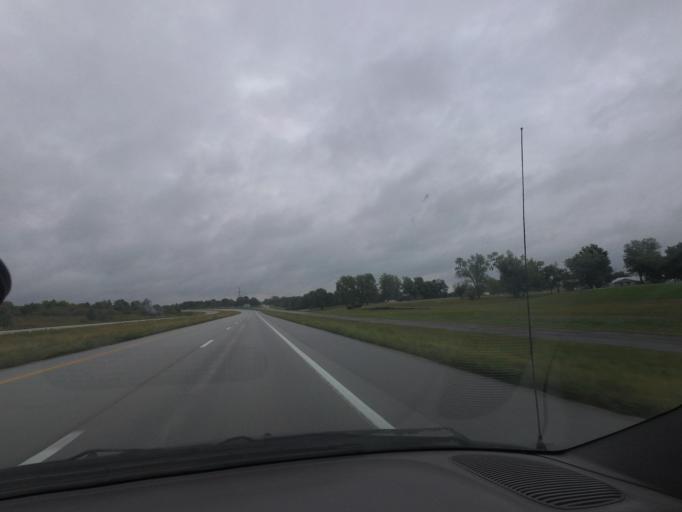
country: US
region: Missouri
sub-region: Marion County
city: Monroe City
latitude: 39.6580
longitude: -91.7566
